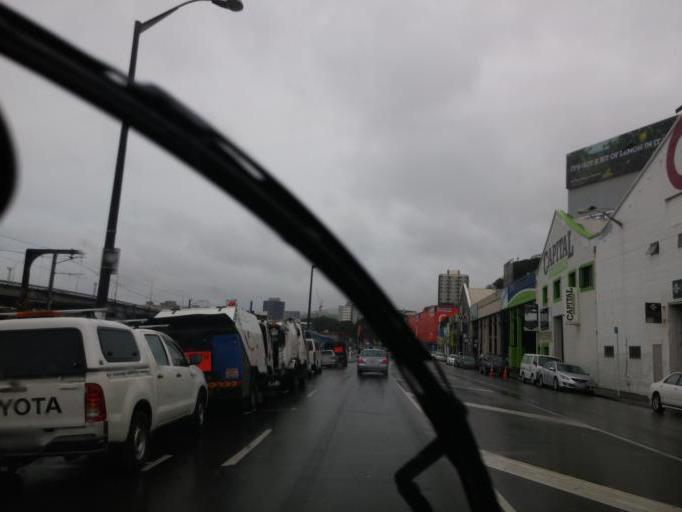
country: NZ
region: Wellington
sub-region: Wellington City
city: Wellington
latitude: -41.2653
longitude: 174.7836
